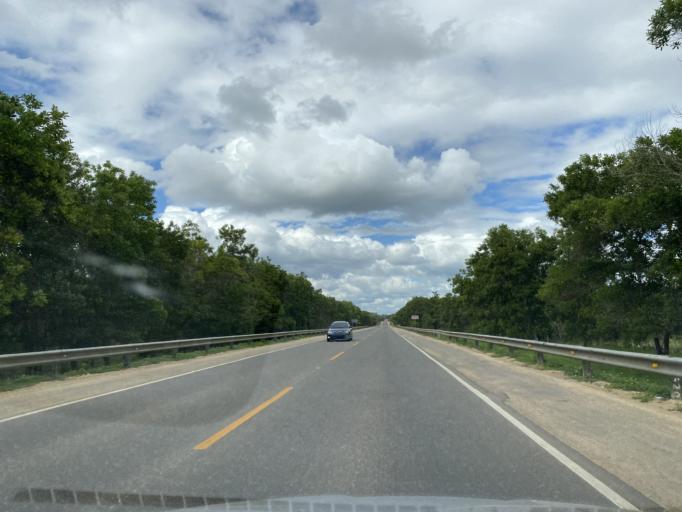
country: DO
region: Santo Domingo
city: Guerra
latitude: 18.5379
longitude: -69.7561
